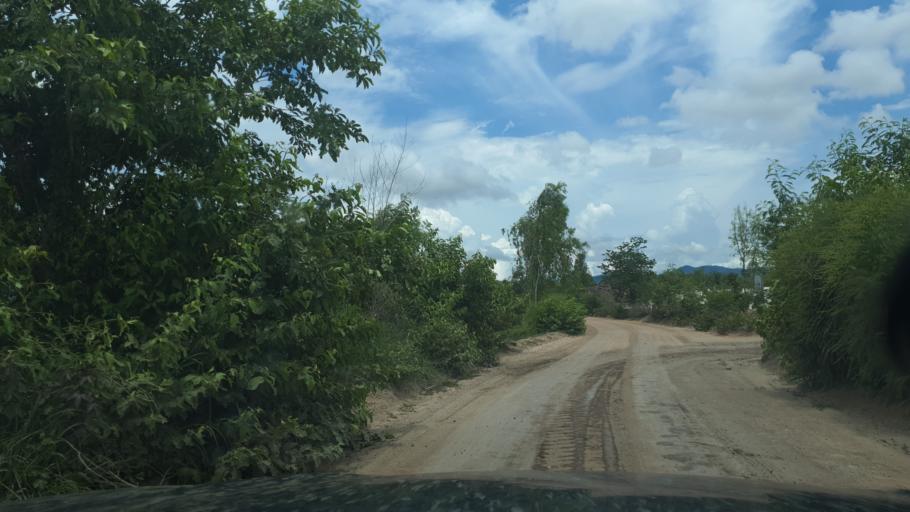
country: TH
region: Lampang
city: Sop Prap
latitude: 17.9355
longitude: 99.3635
